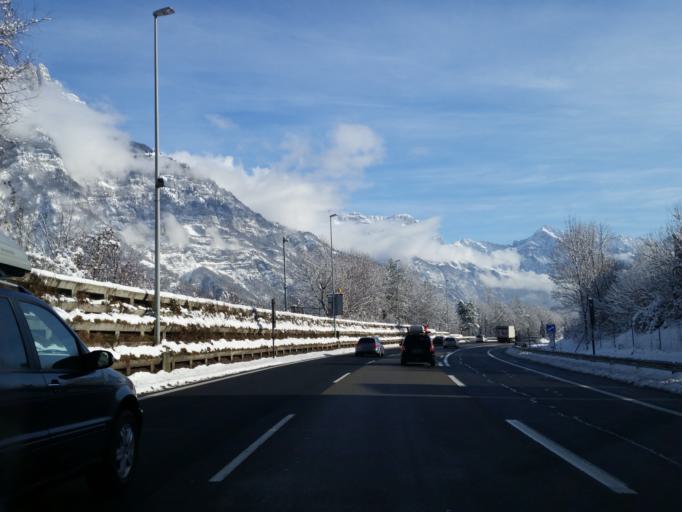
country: CH
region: Saint Gallen
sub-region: Wahlkreis Sarganserland
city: Quarten
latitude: 47.1140
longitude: 9.1875
